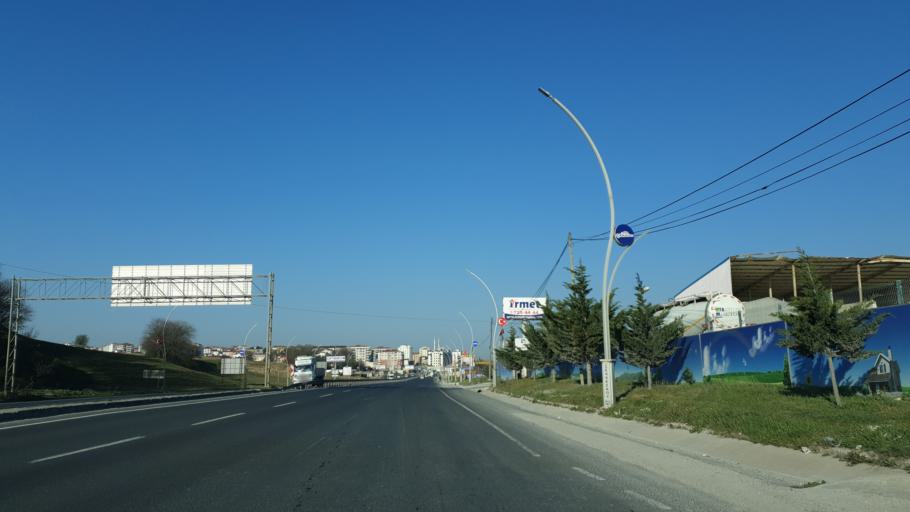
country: TR
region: Tekirdag
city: Cerkezkoey
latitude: 41.2752
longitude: 27.9854
